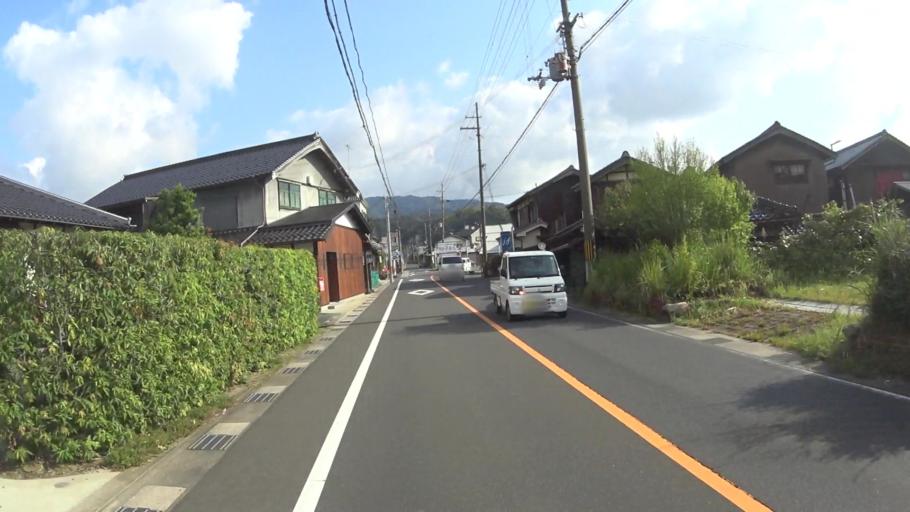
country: JP
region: Kyoto
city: Miyazu
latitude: 35.5698
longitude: 135.1555
